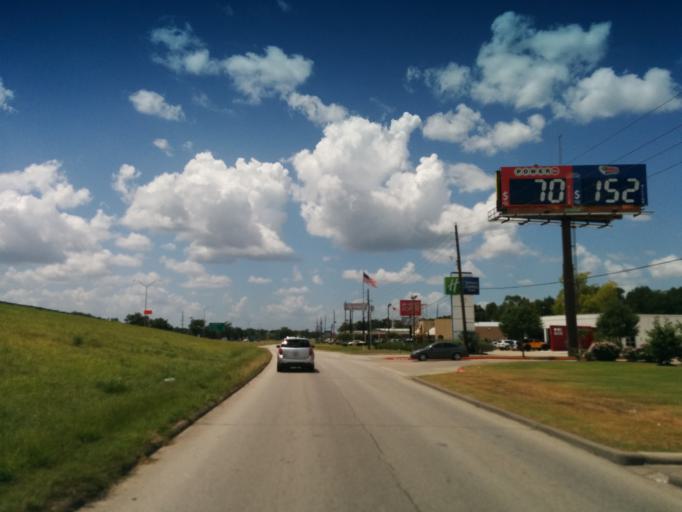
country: US
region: Texas
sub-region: Jefferson County
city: Beaumont
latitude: 30.1341
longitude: -94.1676
